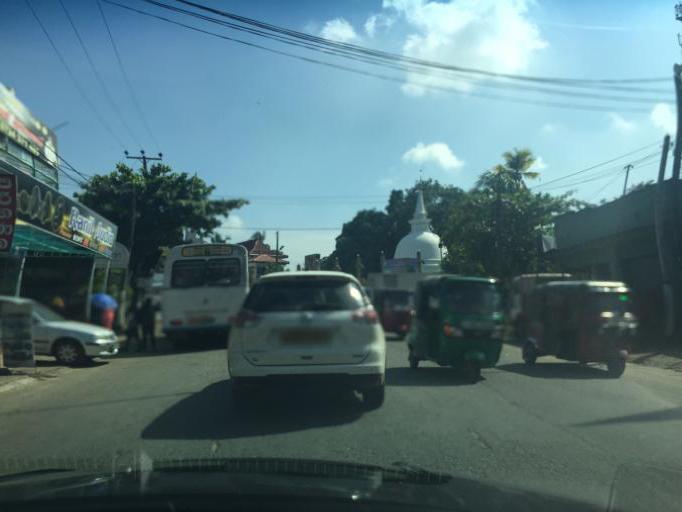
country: LK
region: Western
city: Maharagama
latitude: 6.8036
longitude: 79.9215
